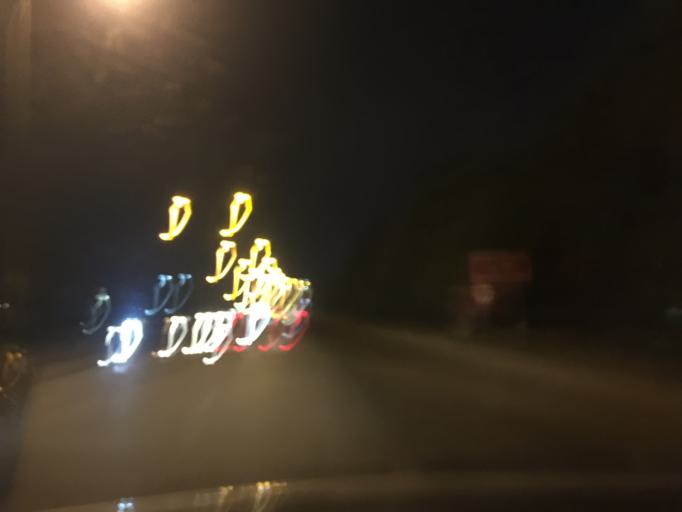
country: JO
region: Amman
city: Wadi as Sir
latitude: 31.9358
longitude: 35.8528
